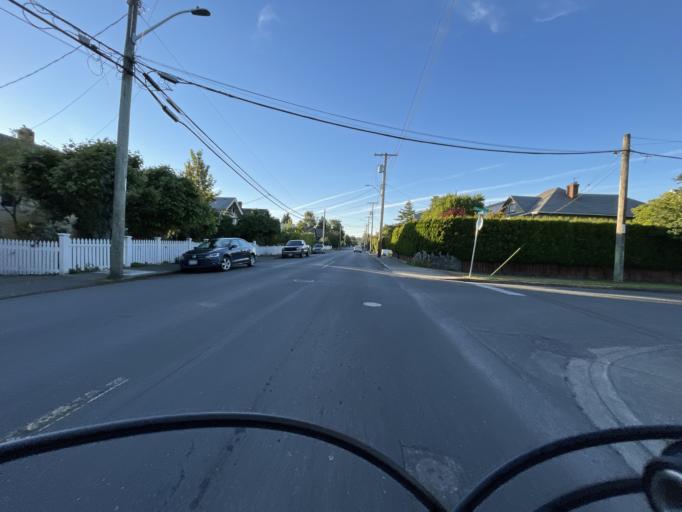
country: CA
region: British Columbia
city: Oak Bay
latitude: 48.4272
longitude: -123.3227
